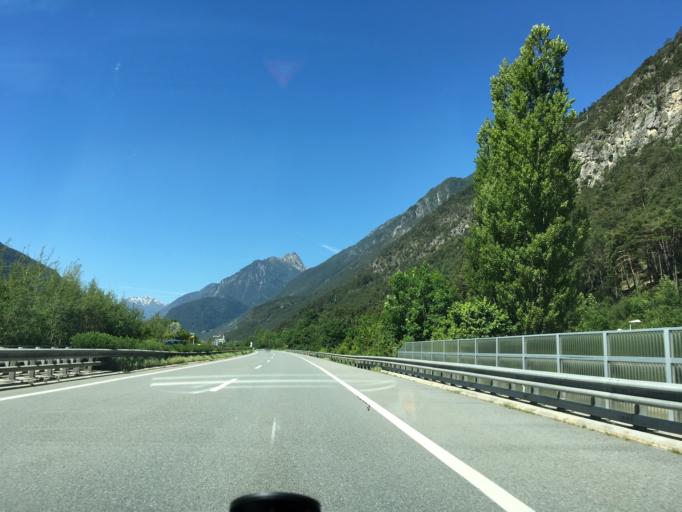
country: AT
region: Tyrol
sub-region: Politischer Bezirk Imst
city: Imsterberg
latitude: 47.2143
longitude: 10.6978
